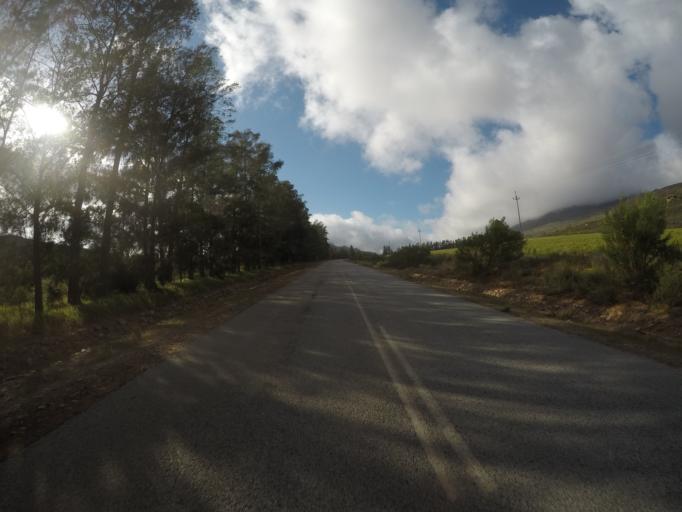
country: ZA
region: Western Cape
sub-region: West Coast District Municipality
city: Clanwilliam
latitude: -32.3476
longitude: 18.8444
